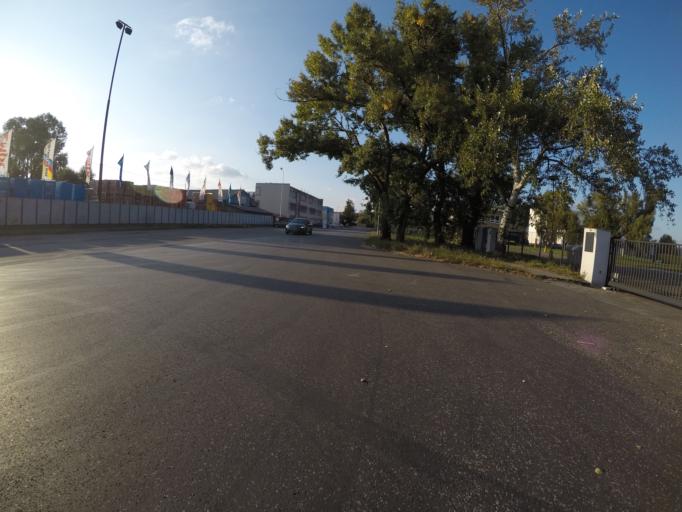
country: SK
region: Bratislavsky
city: Bratislava
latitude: 48.1756
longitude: 17.1752
